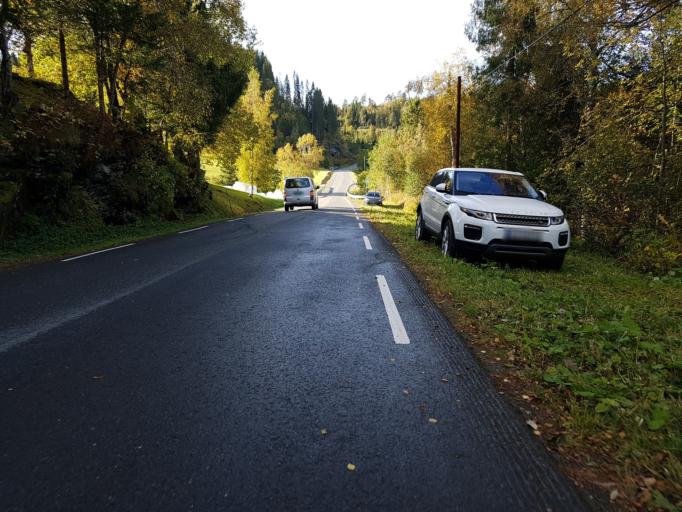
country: NO
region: Sor-Trondelag
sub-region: Klaebu
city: Klaebu
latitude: 63.3449
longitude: 10.5441
